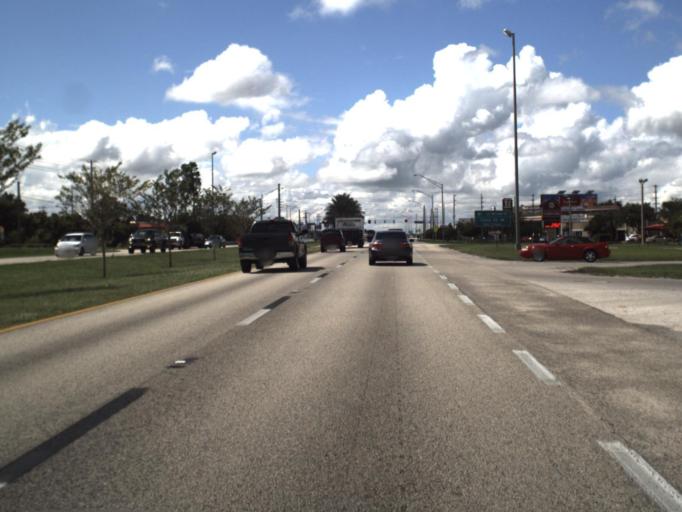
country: US
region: Florida
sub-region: Polk County
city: Medulla
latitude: 27.9779
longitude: -81.9585
